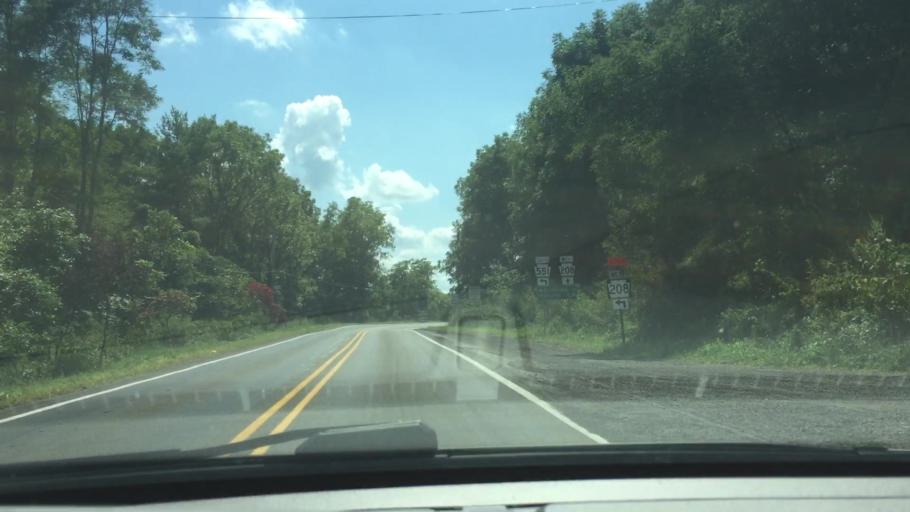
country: US
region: Pennsylvania
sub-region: Lawrence County
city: New Wilmington
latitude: 41.1080
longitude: -80.4384
